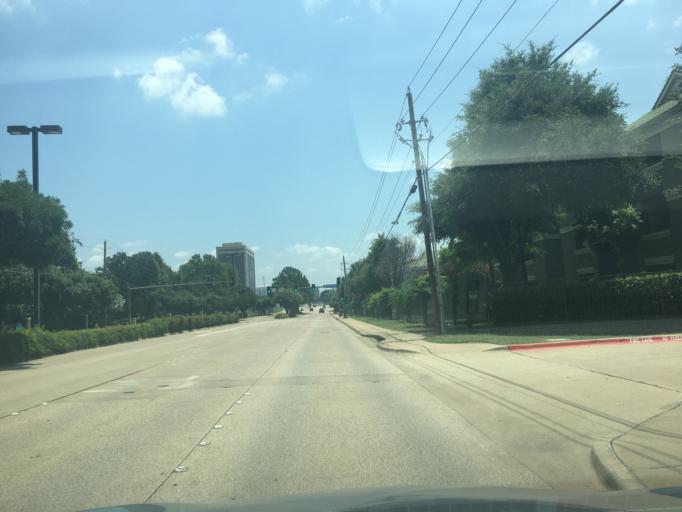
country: US
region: Texas
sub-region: Dallas County
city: Addison
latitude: 32.9398
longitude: -96.8447
